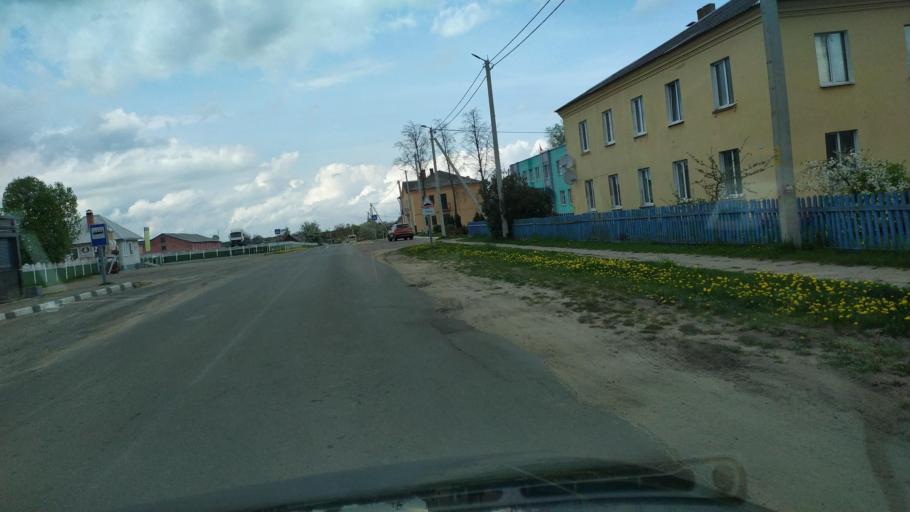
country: BY
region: Brest
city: Pruzhany
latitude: 52.5670
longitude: 24.4187
